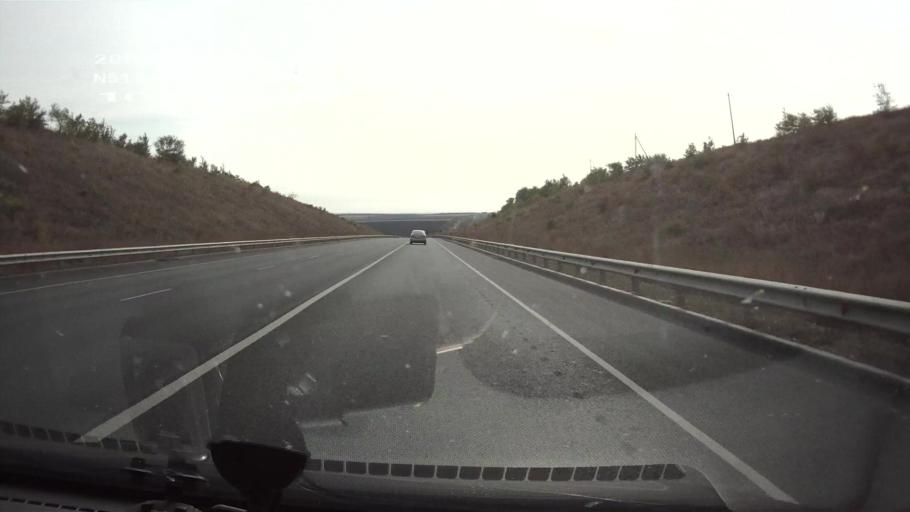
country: RU
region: Saratov
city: Yelshanka
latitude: 51.8885
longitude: 46.5201
